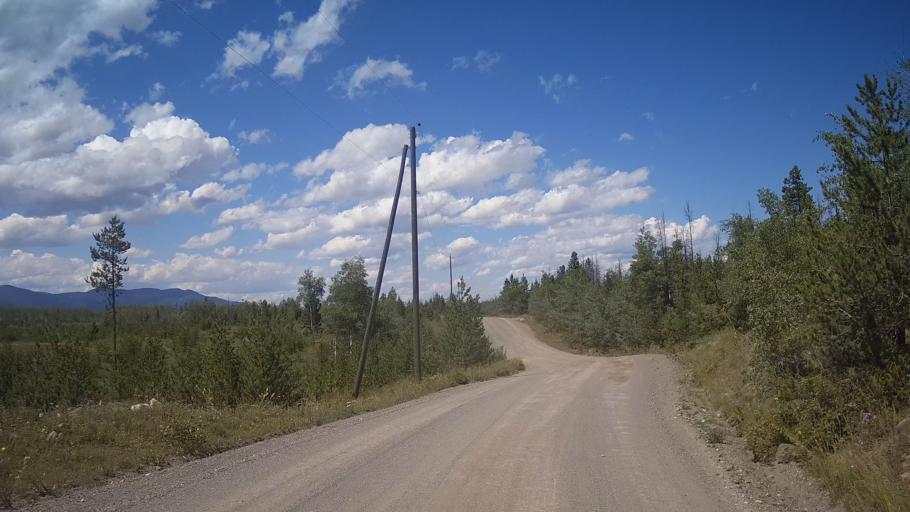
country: CA
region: British Columbia
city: Cache Creek
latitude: 51.2470
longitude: -121.6606
